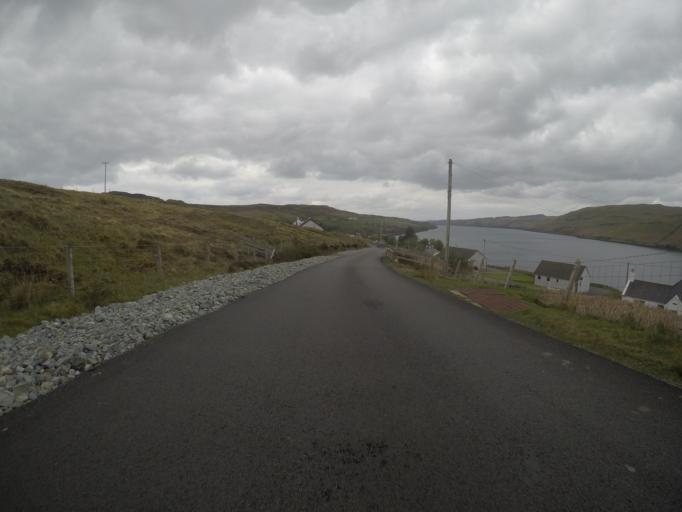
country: GB
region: Scotland
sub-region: Highland
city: Isle of Skye
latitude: 57.2977
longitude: -6.3462
